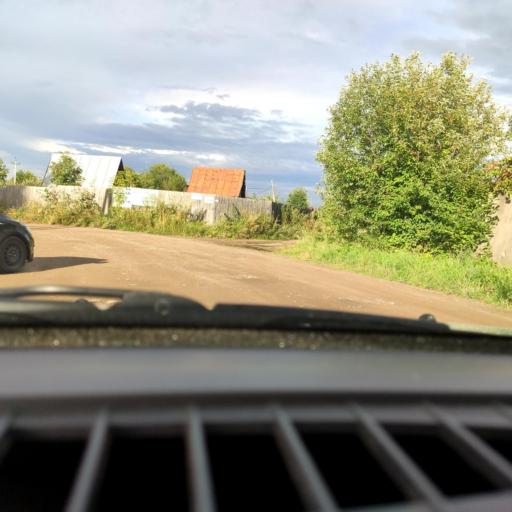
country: RU
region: Perm
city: Kondratovo
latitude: 58.0090
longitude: 56.0716
